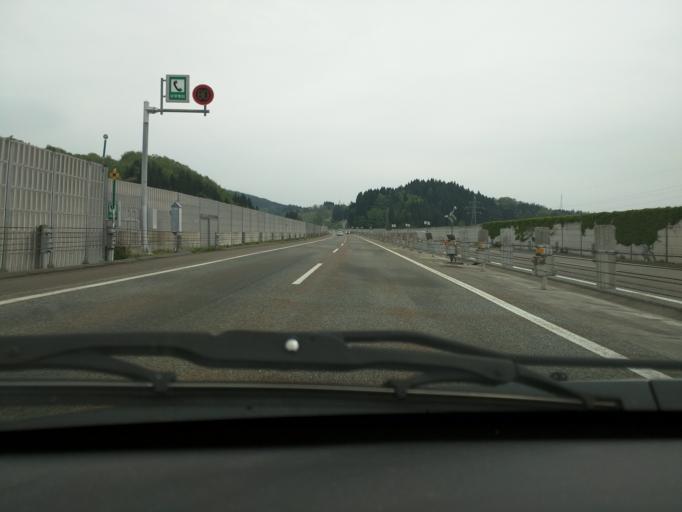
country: JP
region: Niigata
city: Ojiya
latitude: 37.2878
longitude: 138.7847
